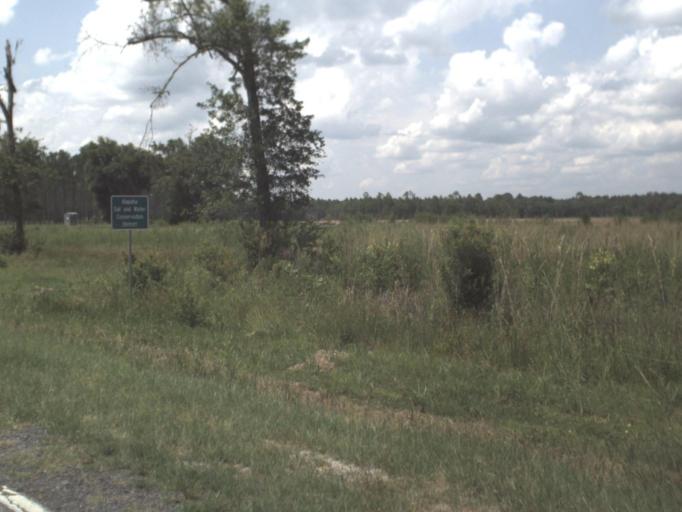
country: US
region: Georgia
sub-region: Echols County
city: Statenville
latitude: 30.6231
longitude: -83.1187
